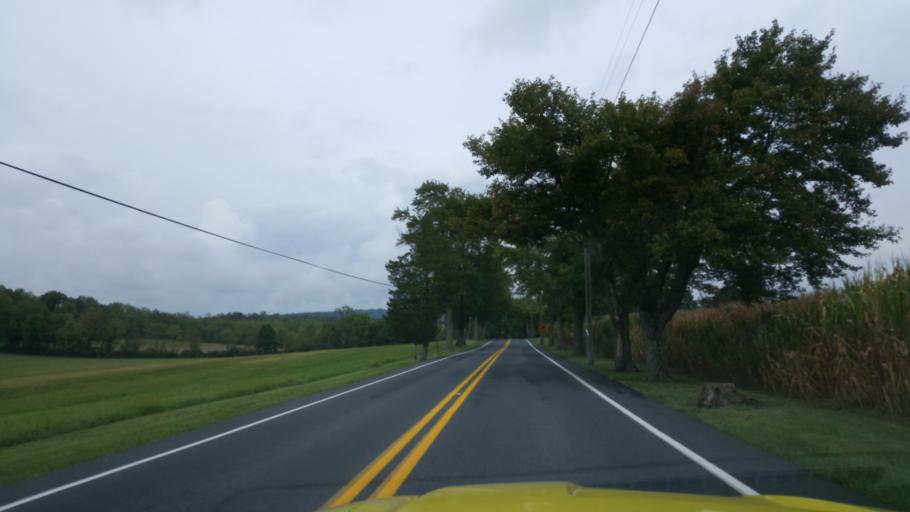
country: US
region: Pennsylvania
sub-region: Lebanon County
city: Campbelltown
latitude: 40.2403
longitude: -76.5314
